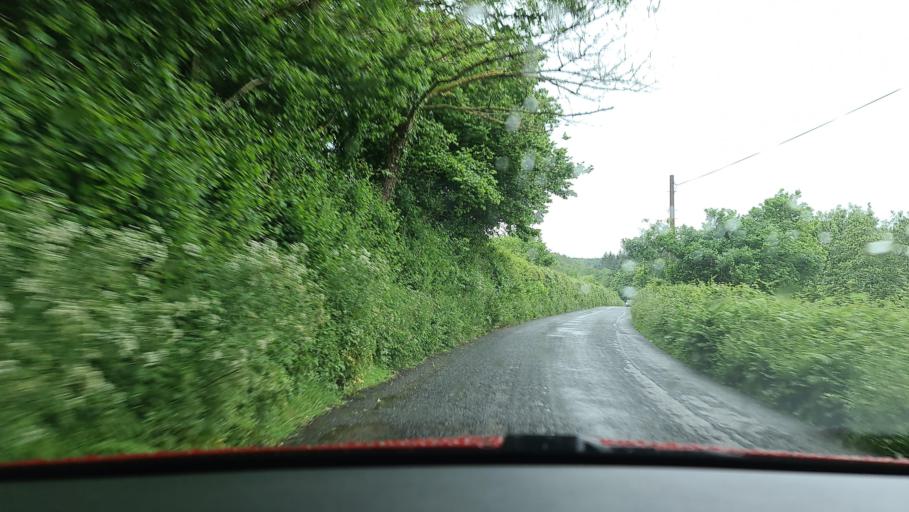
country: GB
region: England
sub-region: Cornwall
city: Liskeard
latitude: 50.4635
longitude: -4.5576
